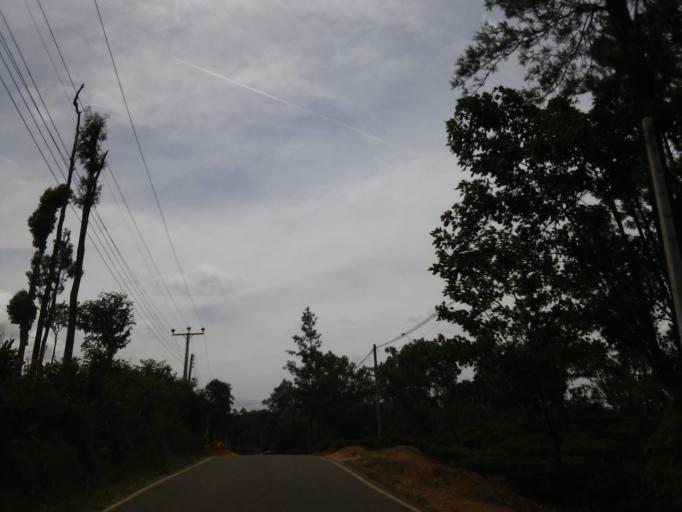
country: LK
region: Uva
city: Haputale
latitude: 6.8491
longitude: 81.0239
